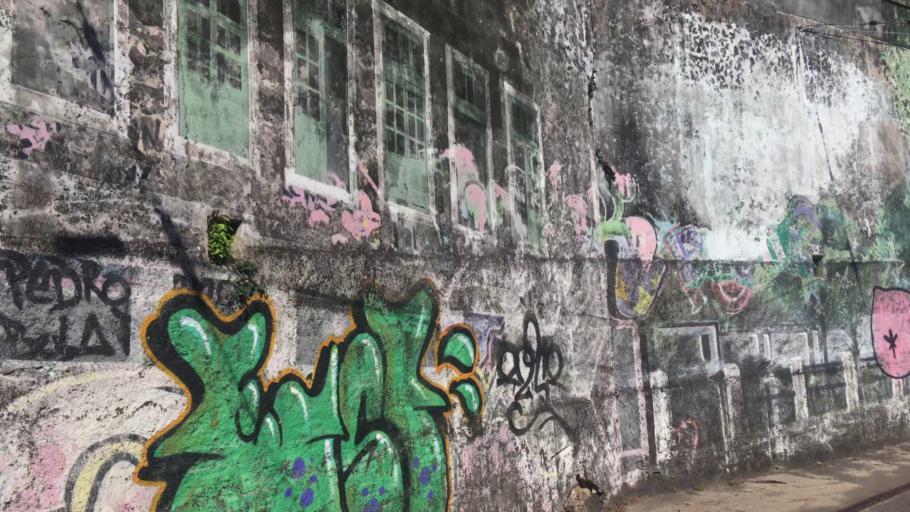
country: BR
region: Rio de Janeiro
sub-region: Rio De Janeiro
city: Rio de Janeiro
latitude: -22.9230
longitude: -43.1877
